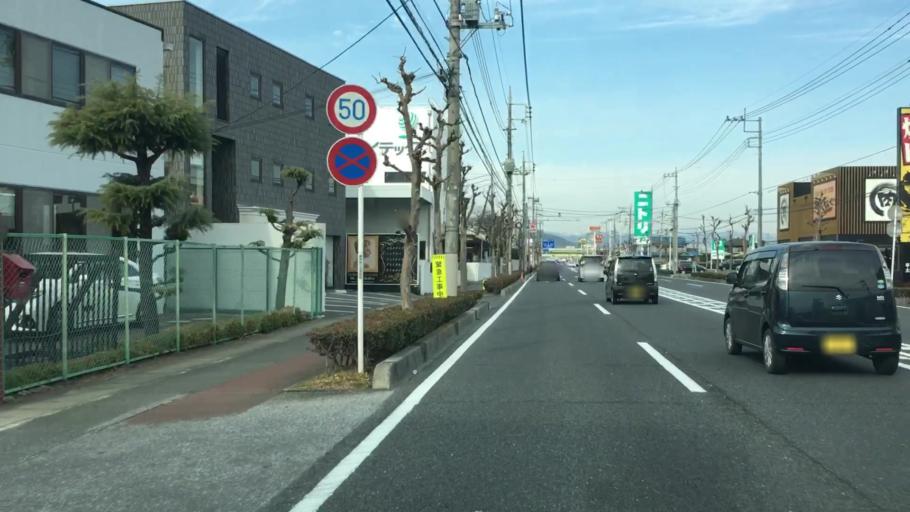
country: JP
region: Gunma
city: Ota
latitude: 36.2648
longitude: 139.3769
